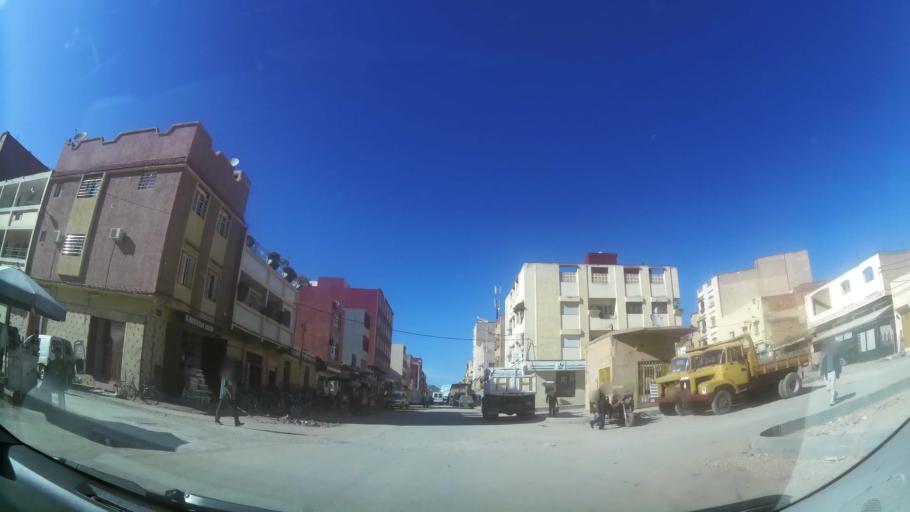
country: MA
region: Oriental
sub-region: Berkane-Taourirt
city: Ahfir
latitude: 34.9514
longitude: -2.1004
